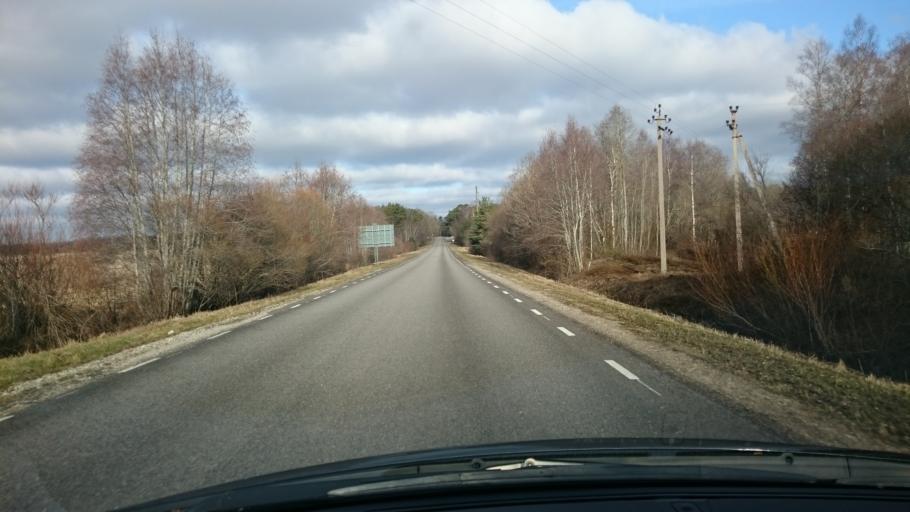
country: EE
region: Harju
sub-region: Keila linn
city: Keila
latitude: 59.3286
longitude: 24.3731
